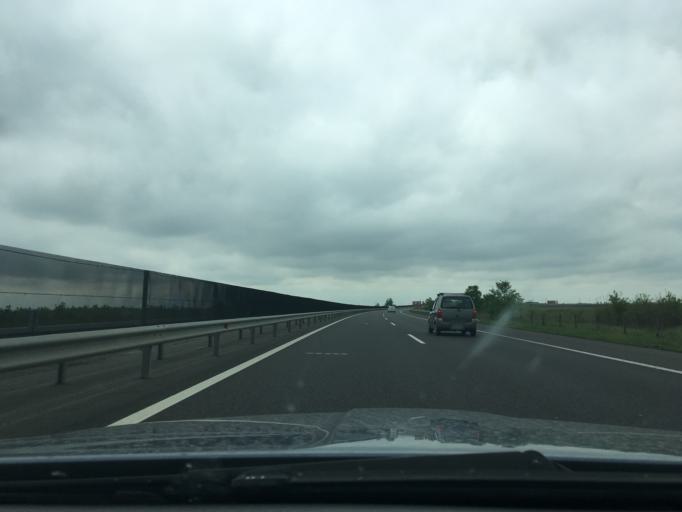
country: HU
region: Hajdu-Bihar
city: Polgar
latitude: 47.8133
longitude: 21.1574
